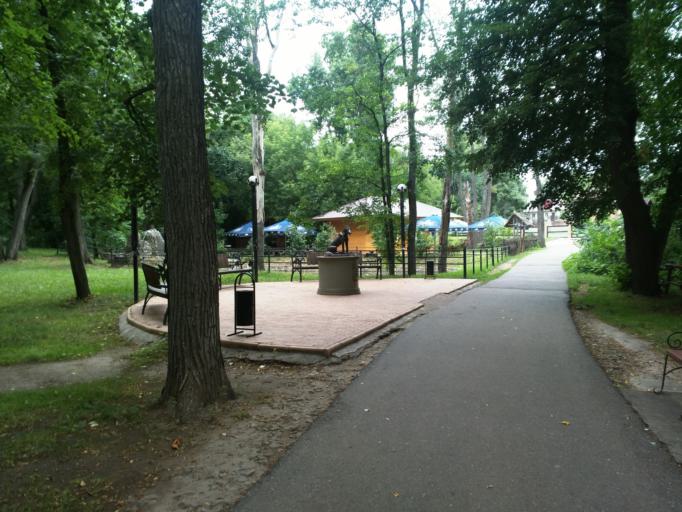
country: RU
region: Tatarstan
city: Yelabuga
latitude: 55.7576
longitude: 52.0455
